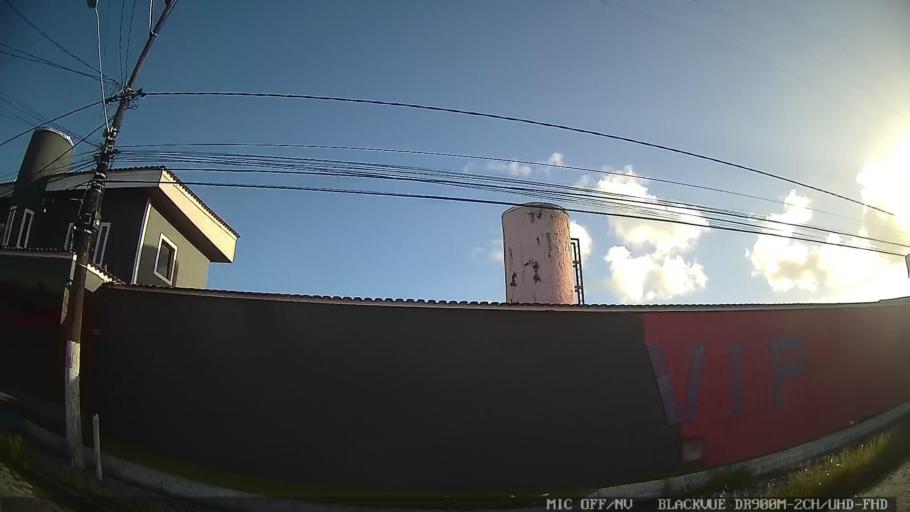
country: BR
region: Sao Paulo
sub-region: Itanhaem
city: Itanhaem
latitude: -24.1394
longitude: -46.7141
